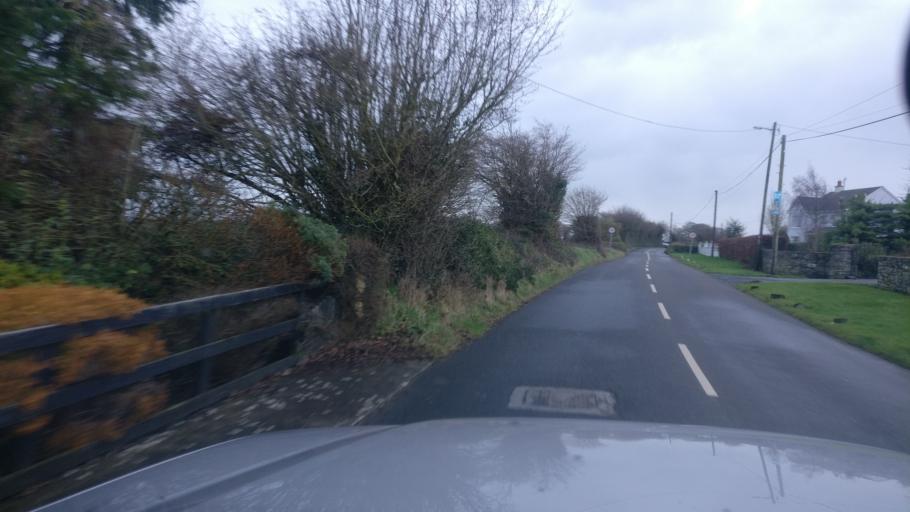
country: IE
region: Munster
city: Nenagh Bridge
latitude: 52.9915
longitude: -8.1201
